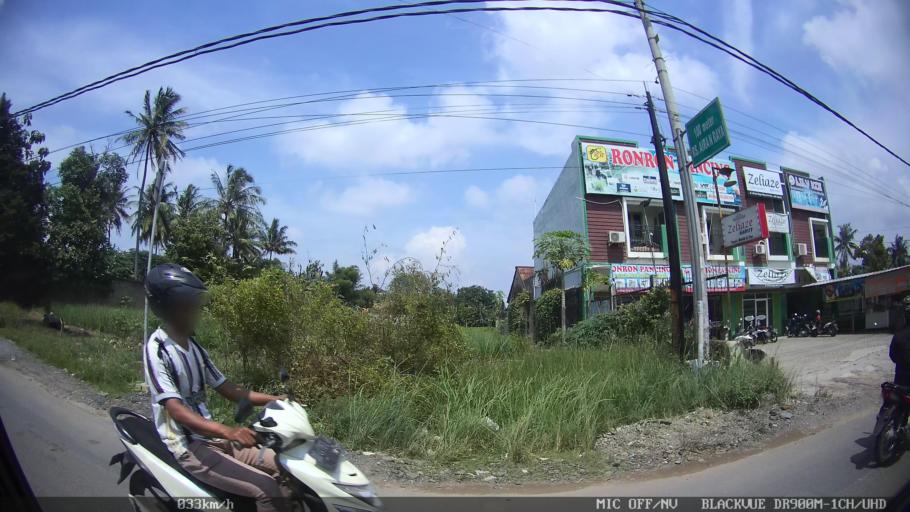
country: ID
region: Lampung
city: Kedaton
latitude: -5.3515
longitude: 105.2994
